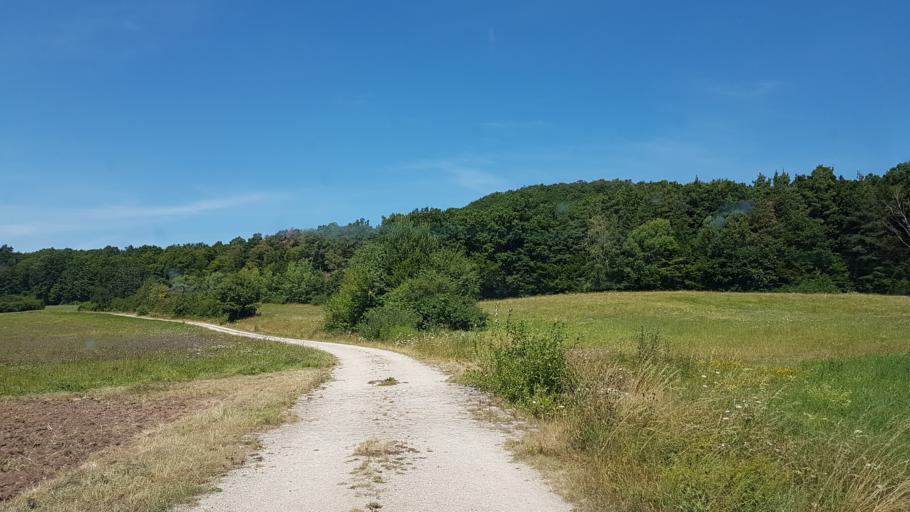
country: DE
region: Bavaria
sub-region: Regierungsbezirk Unterfranken
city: Sand
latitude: 49.9546
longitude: 10.5899
